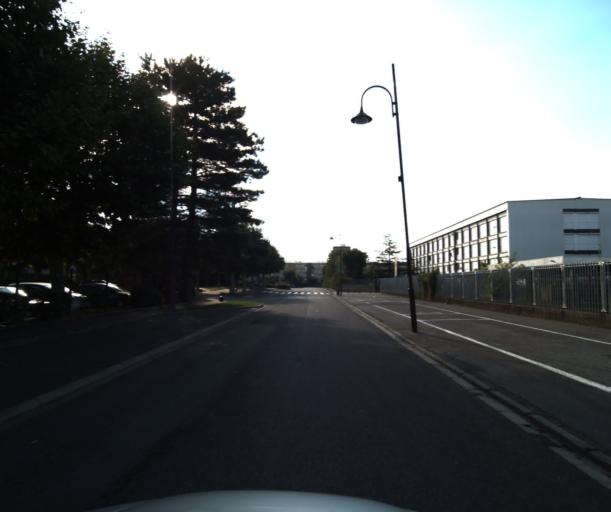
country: FR
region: Midi-Pyrenees
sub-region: Departement de la Haute-Garonne
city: Muret
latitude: 43.4700
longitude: 1.3345
